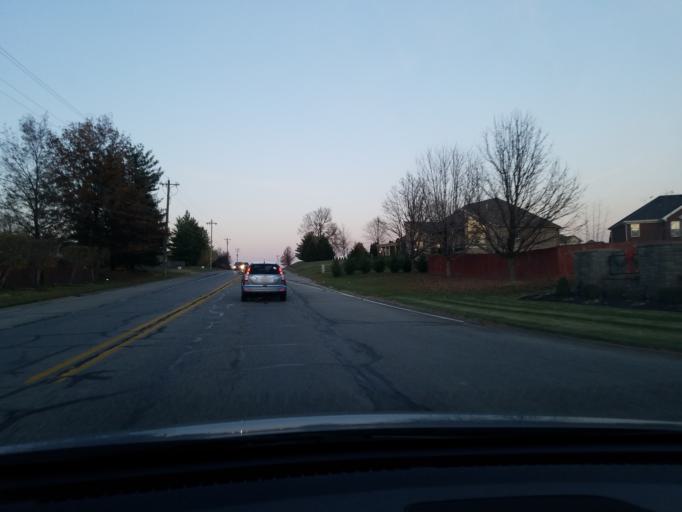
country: US
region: Indiana
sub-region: Clark County
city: Sellersburg
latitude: 38.3636
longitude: -85.7809
